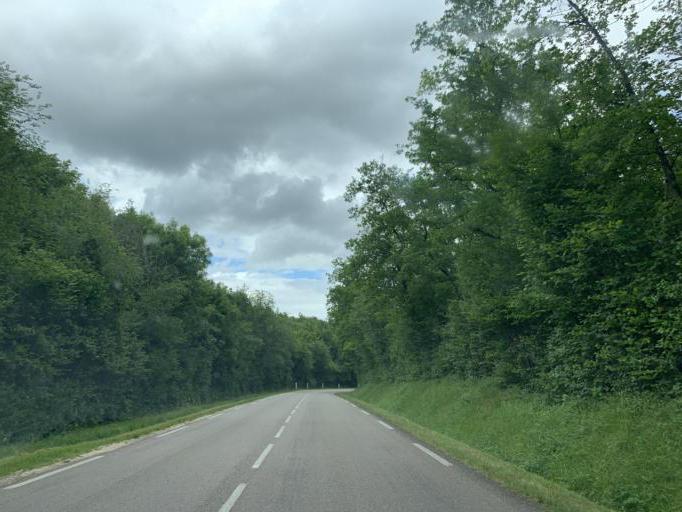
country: FR
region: Bourgogne
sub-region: Departement de l'Yonne
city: Chablis
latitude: 47.7402
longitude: 3.8180
